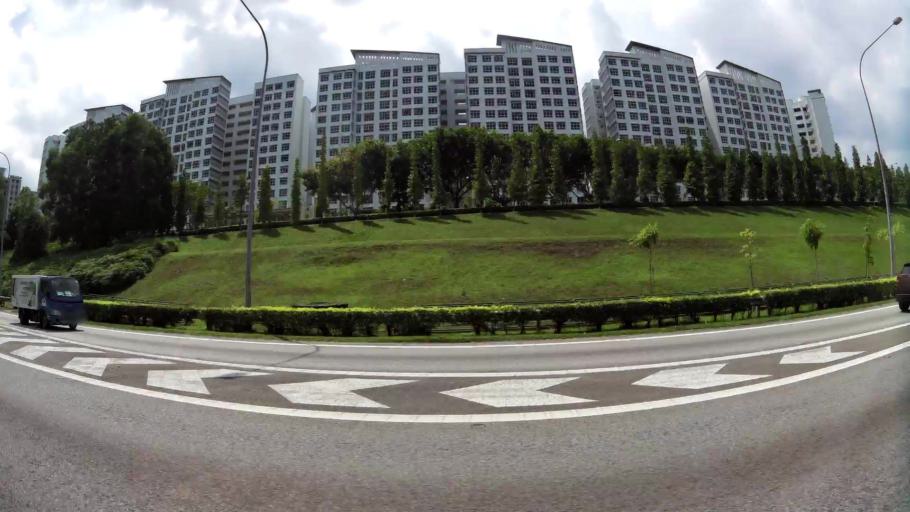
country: MY
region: Johor
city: Kampung Pasir Gudang Baru
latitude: 1.3996
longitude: 103.8972
